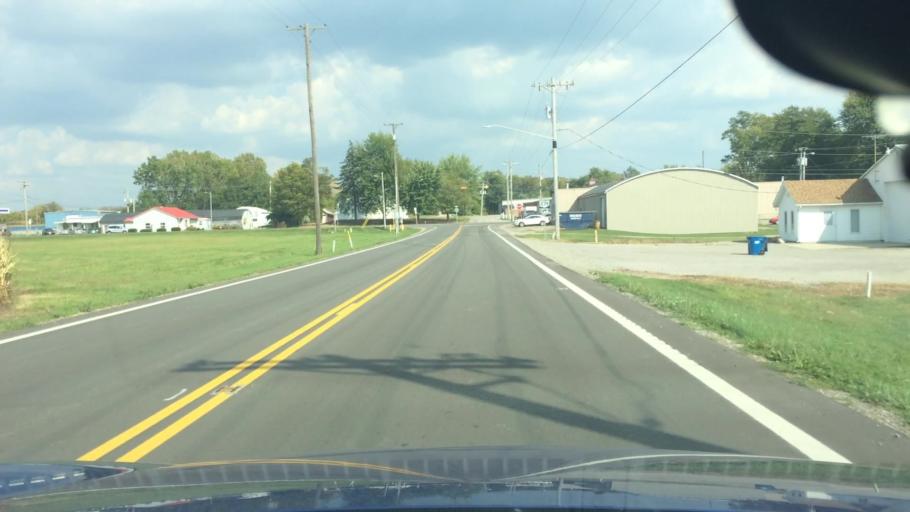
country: US
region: Ohio
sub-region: Logan County
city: Northwood
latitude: 40.4470
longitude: -83.8082
